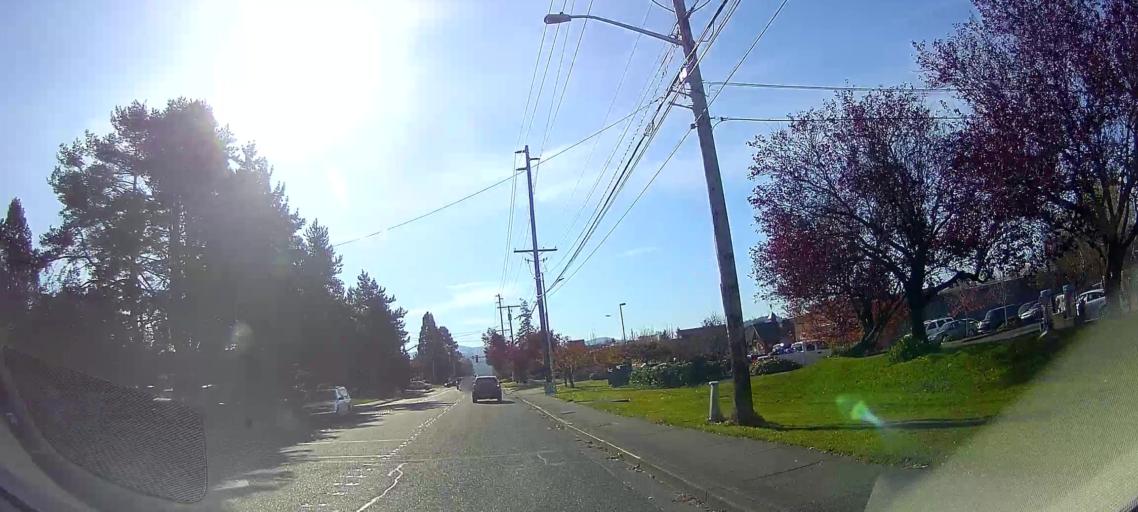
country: US
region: Washington
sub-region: Whatcom County
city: Bellingham
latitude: 48.7723
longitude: -122.4577
